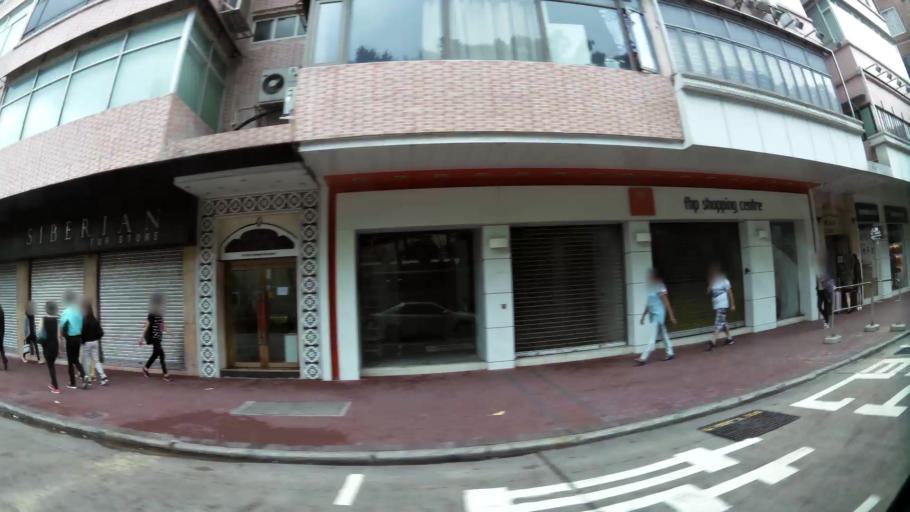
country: HK
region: Wanchai
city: Wan Chai
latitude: 22.2978
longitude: 114.1754
